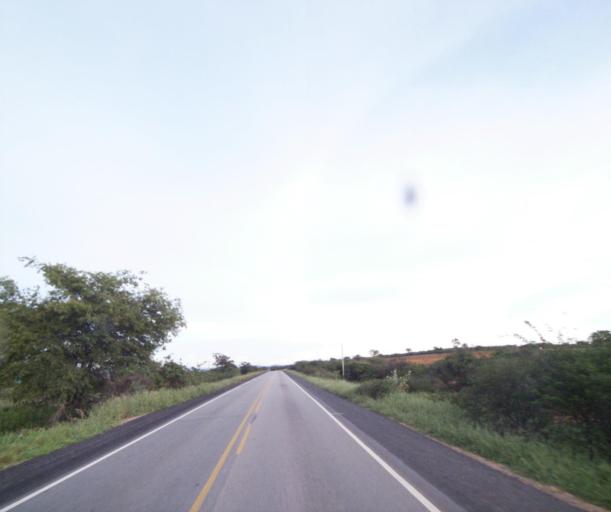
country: BR
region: Bahia
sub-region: Brumado
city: Brumado
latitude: -14.2515
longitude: -41.8491
